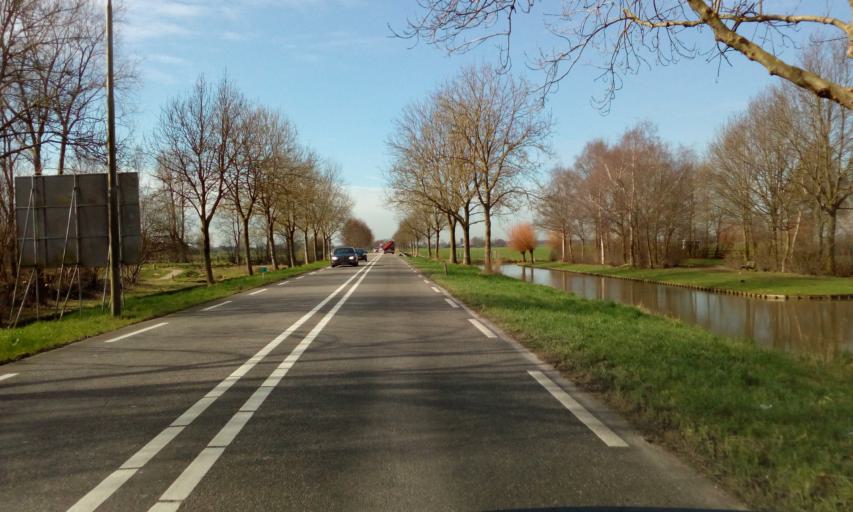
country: NL
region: South Holland
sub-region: Gemeente Nieuwkoop
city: Nieuwkoop
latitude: 52.1514
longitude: 4.7688
